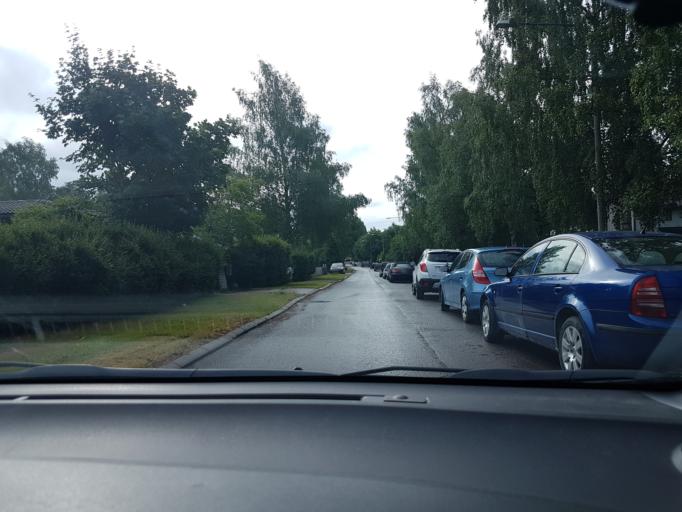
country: FI
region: Uusimaa
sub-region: Helsinki
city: Vantaa
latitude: 60.2396
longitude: 25.0144
